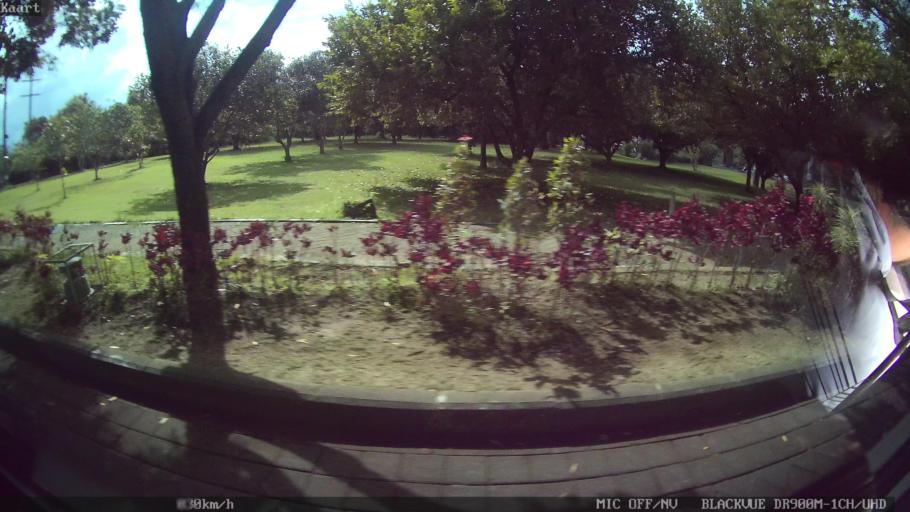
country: ID
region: Bali
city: Banjar Karangsuling
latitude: -8.6038
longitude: 115.1800
